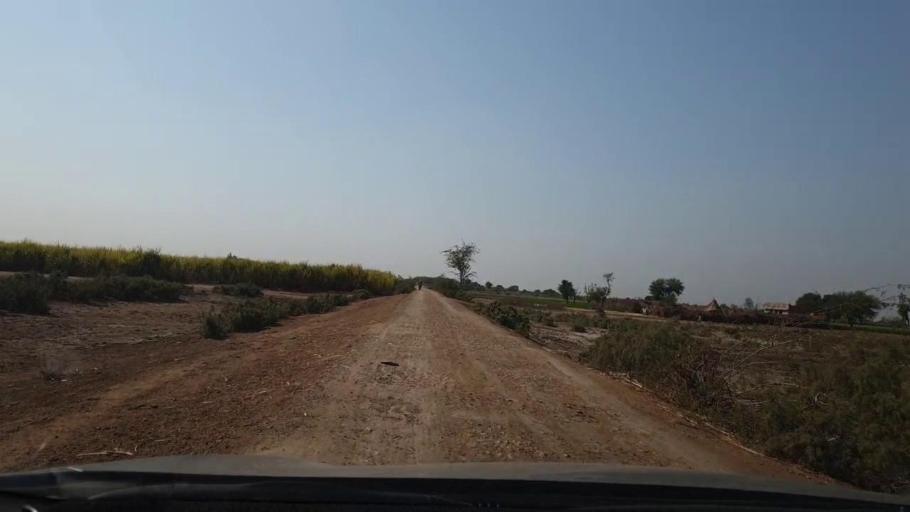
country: PK
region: Sindh
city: Mirpur Khas
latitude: 25.6019
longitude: 68.8732
